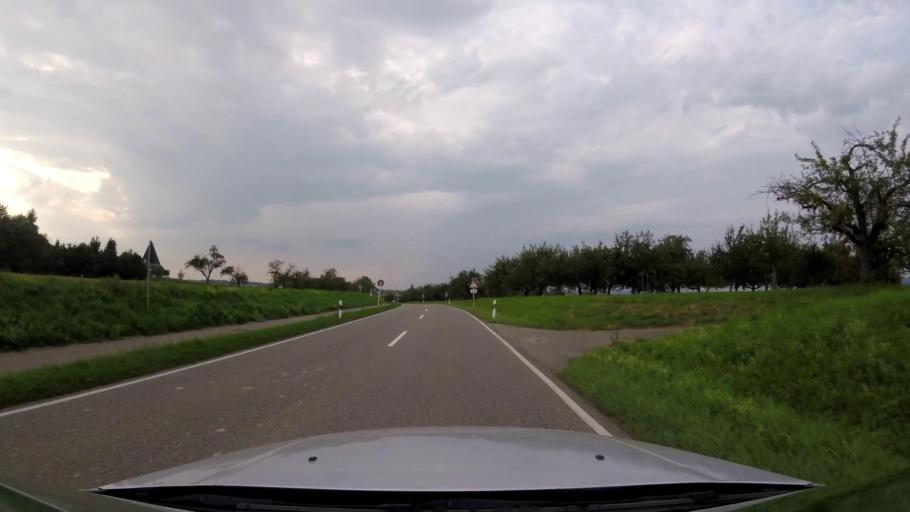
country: DE
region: Baden-Wuerttemberg
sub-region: Regierungsbezirk Stuttgart
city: Allmersbach im Tal
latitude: 48.9215
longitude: 9.4598
